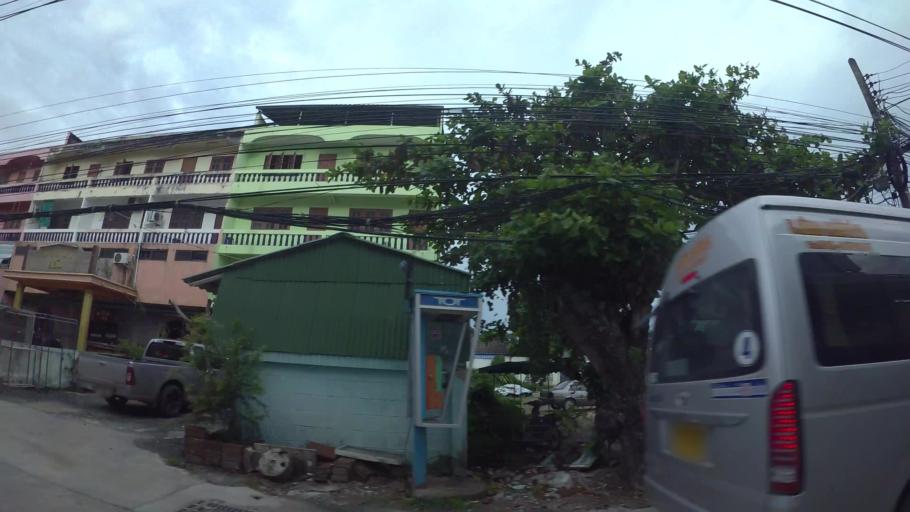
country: TH
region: Rayong
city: Rayong
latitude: 12.6880
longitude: 101.2658
